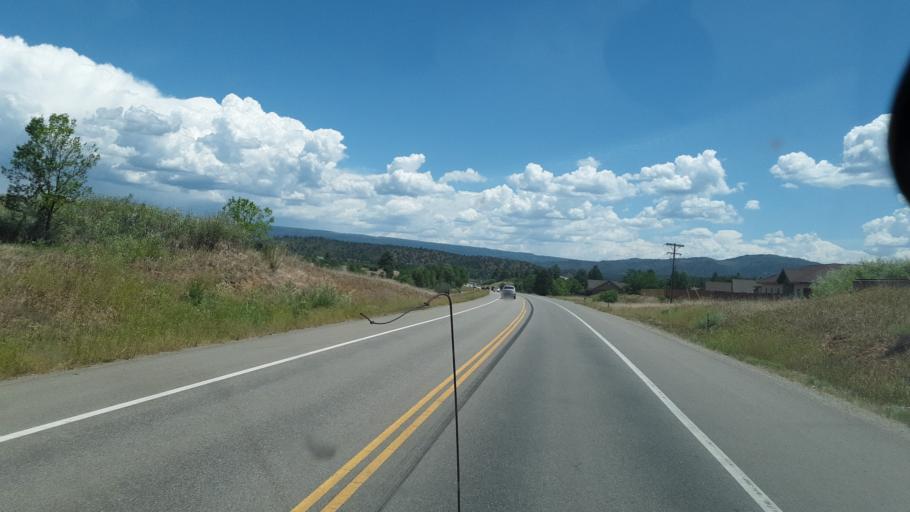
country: US
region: Colorado
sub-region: La Plata County
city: Bayfield
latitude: 37.2348
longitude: -107.5860
